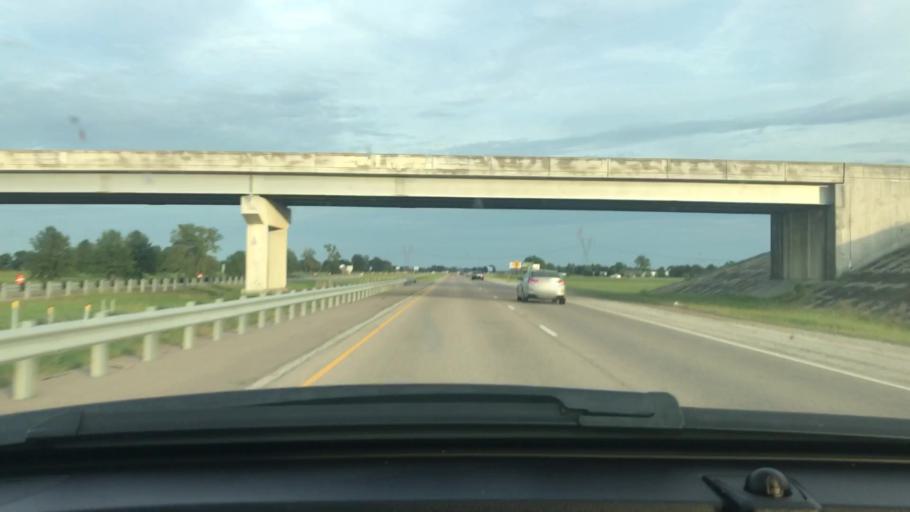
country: US
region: Arkansas
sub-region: Craighead County
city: Bay
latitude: 35.7754
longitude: -90.5863
